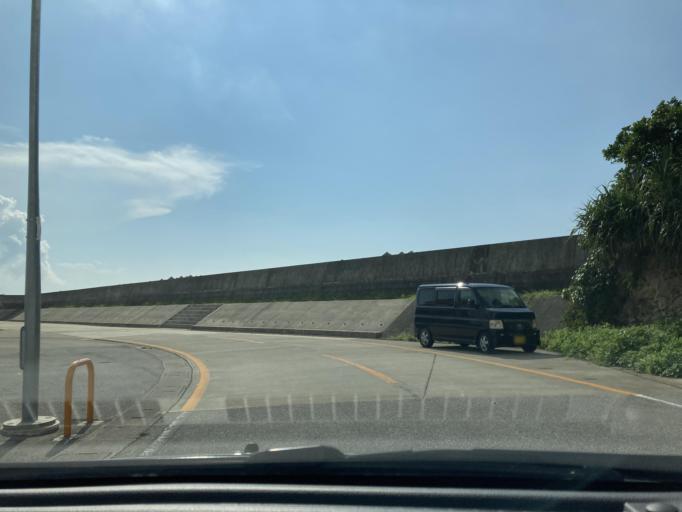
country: JP
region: Okinawa
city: Itoman
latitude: 26.1295
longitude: 127.7758
